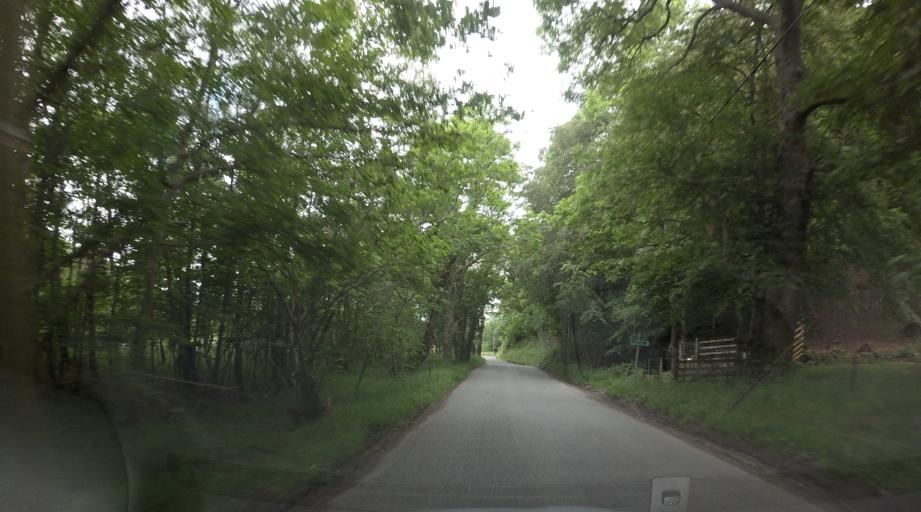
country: GB
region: Scotland
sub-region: Perth and Kinross
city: Aberfeldy
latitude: 56.7017
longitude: -4.1730
